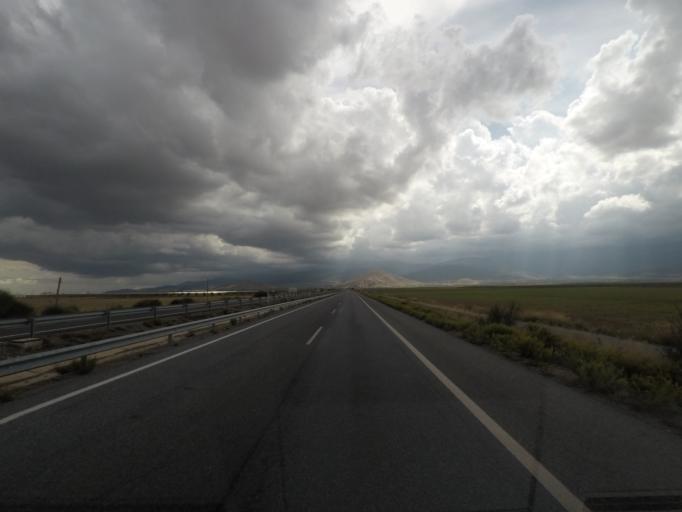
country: ES
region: Andalusia
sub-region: Provincia de Granada
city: Albunan
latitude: 37.2227
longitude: -3.0783
